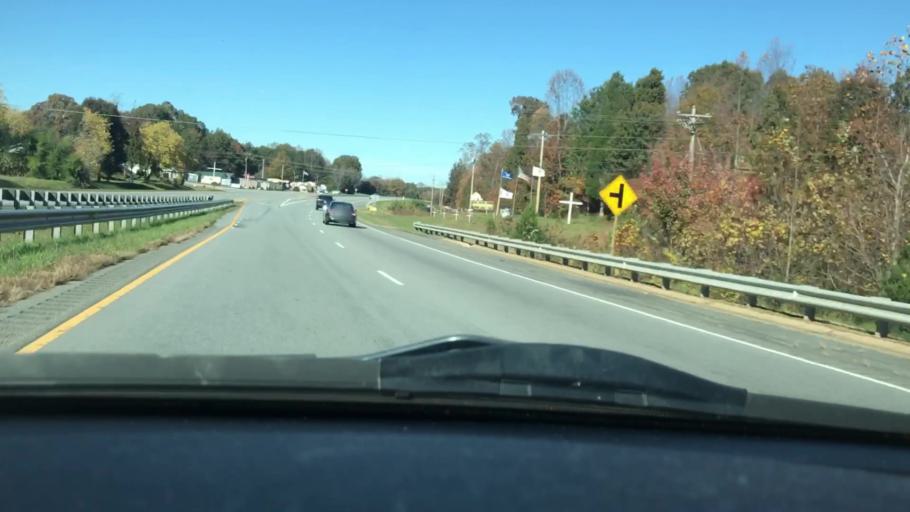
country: US
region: North Carolina
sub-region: Rockingham County
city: Madison
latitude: 36.3293
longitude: -79.9466
